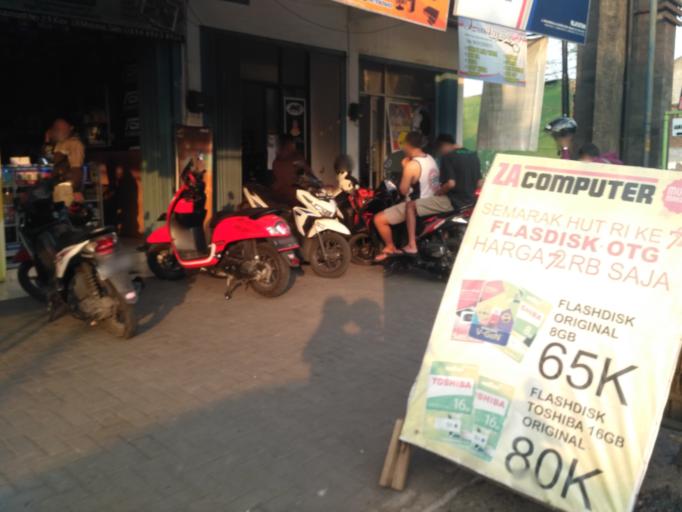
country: ID
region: East Java
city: Kepuh
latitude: -8.0050
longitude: 112.6181
